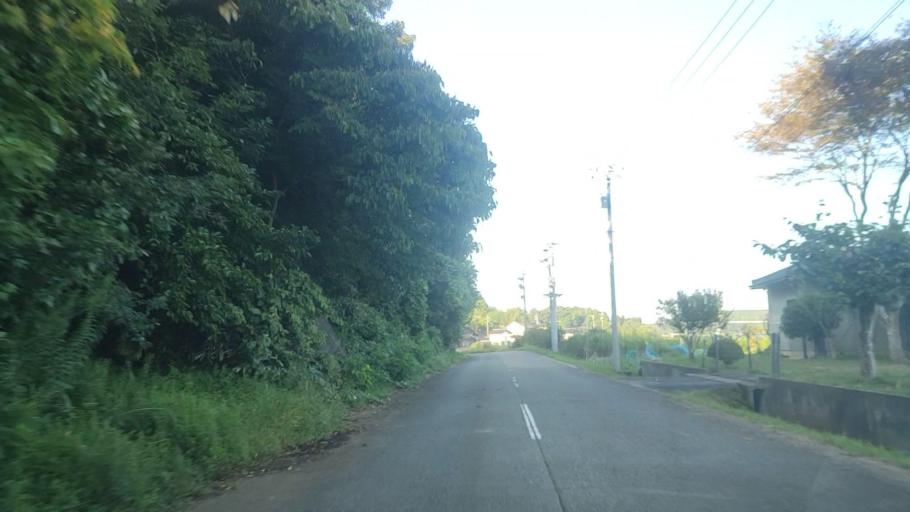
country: JP
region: Ishikawa
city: Nanao
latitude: 37.1268
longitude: 136.8960
